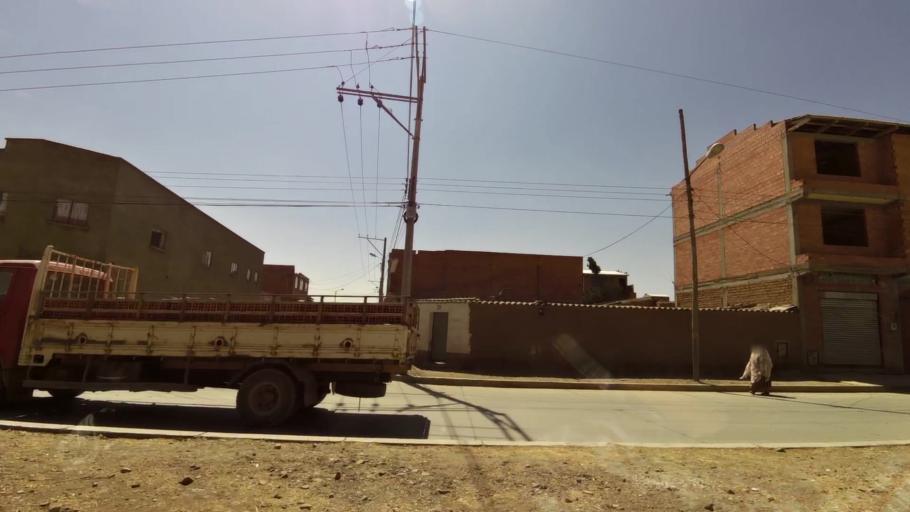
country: BO
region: La Paz
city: La Paz
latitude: -16.5375
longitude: -68.1573
